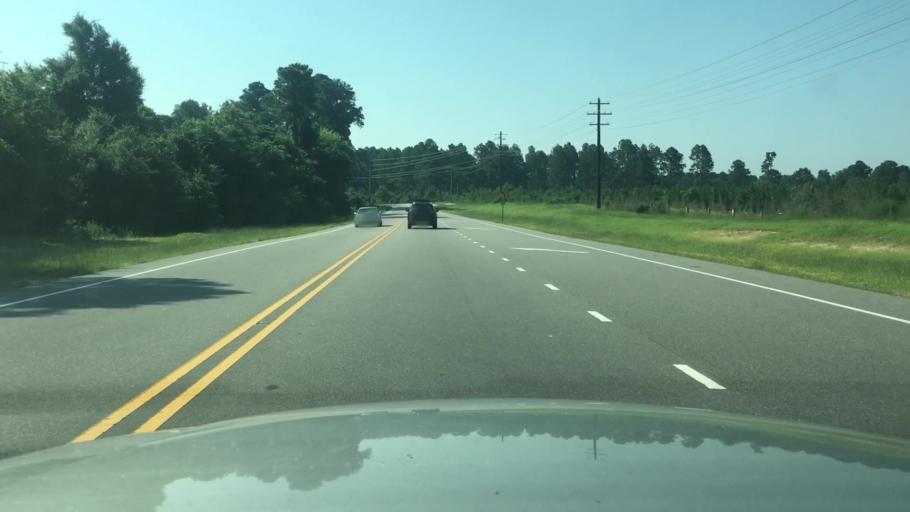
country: US
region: North Carolina
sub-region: Cumberland County
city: Spring Lake
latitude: 35.1357
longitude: -78.9036
